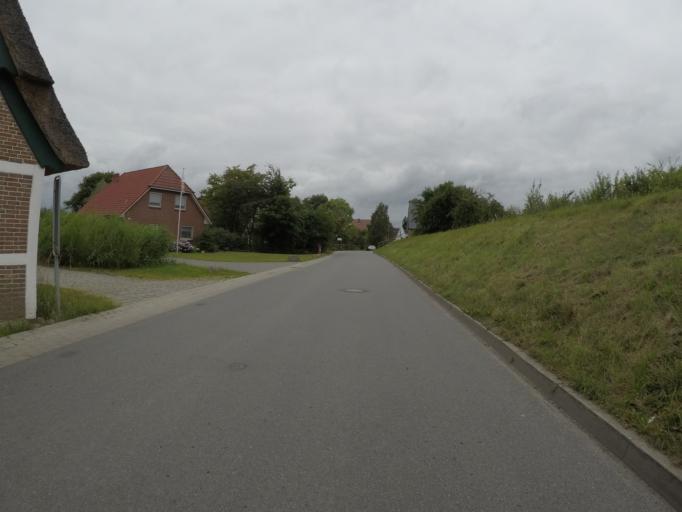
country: DE
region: Lower Saxony
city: Guderhandviertel
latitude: 53.5529
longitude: 9.6066
